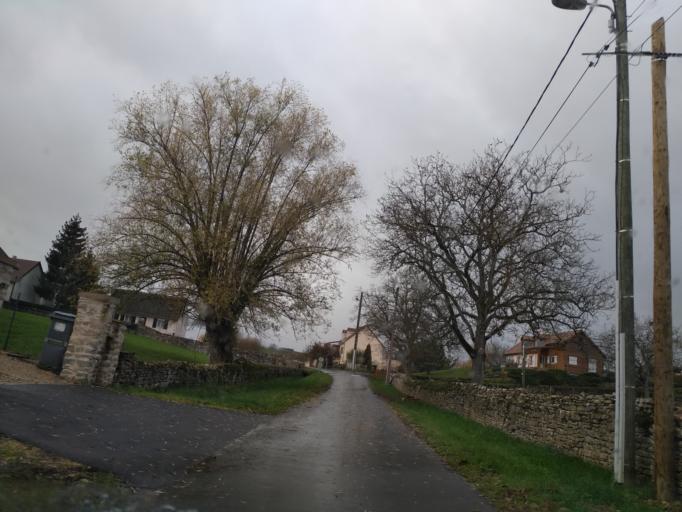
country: FR
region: Bourgogne
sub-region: Departement de Saone-et-Loire
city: Saint-Leger-sur-Dheune
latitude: 46.8691
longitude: 4.6856
